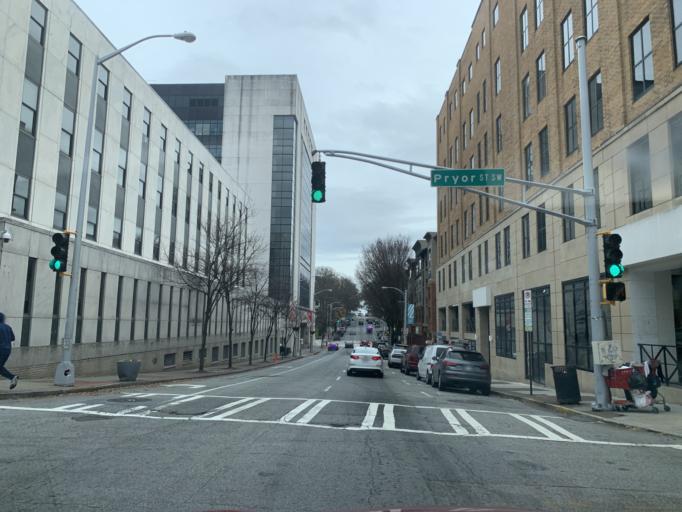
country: US
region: Georgia
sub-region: Fulton County
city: Atlanta
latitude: 33.7503
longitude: -84.3919
